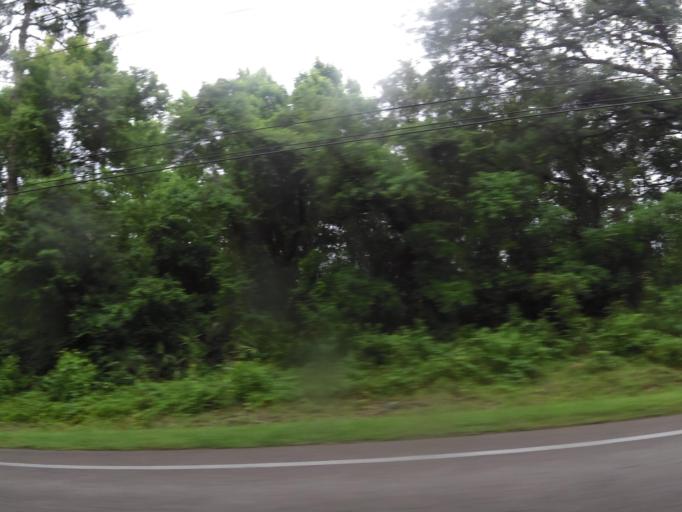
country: US
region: Florida
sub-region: Saint Johns County
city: Saint Augustine
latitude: 29.9127
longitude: -81.3679
